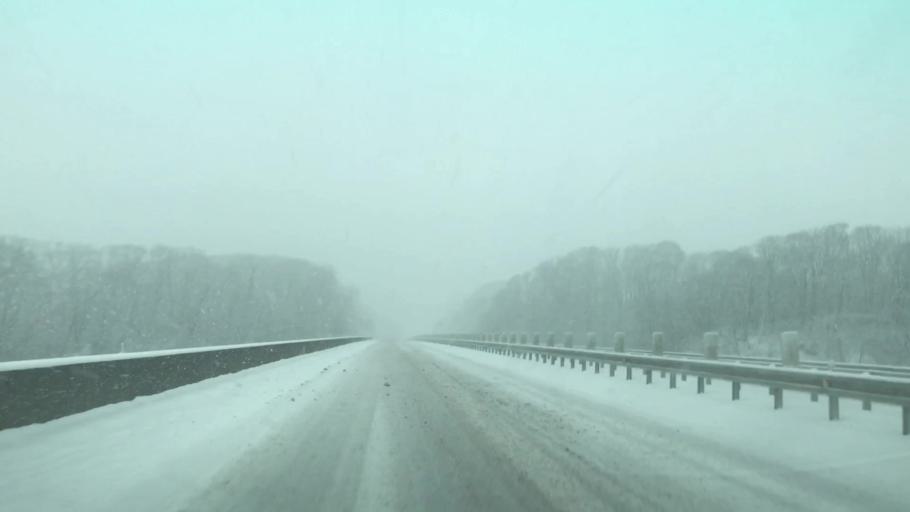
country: JP
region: Hokkaido
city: Muroran
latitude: 42.4409
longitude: 141.1418
